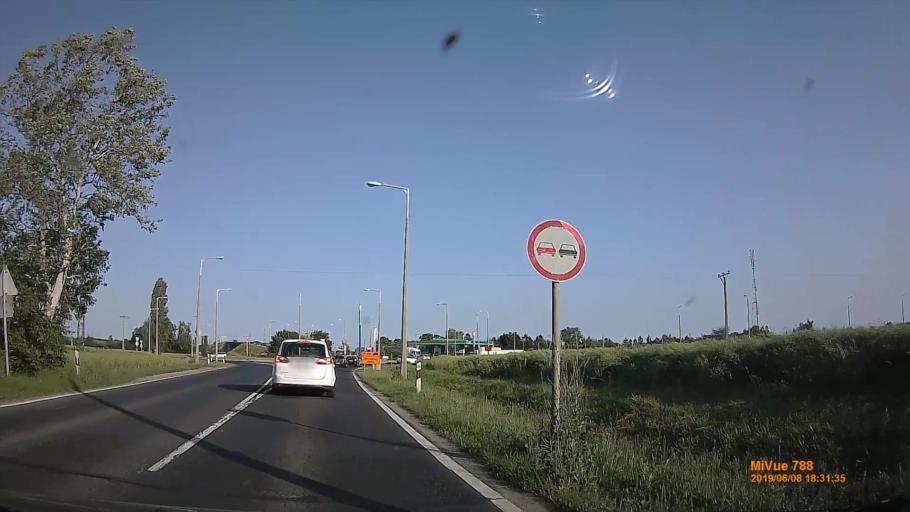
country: HU
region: Vas
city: Sarvar
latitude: 47.3614
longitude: 16.8968
